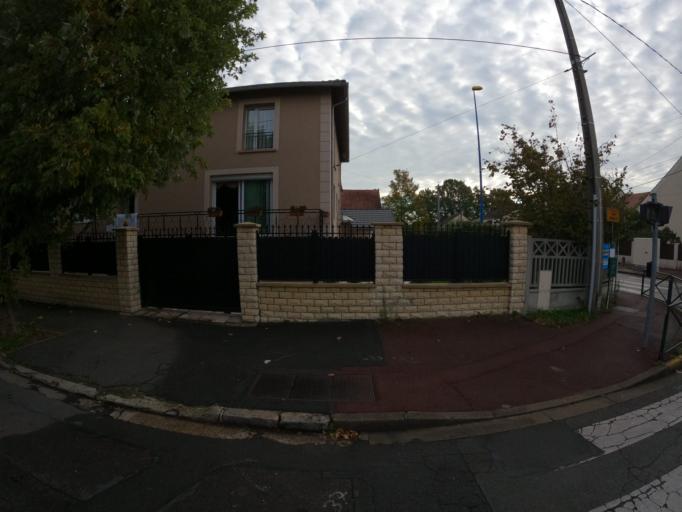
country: FR
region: Ile-de-France
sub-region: Departement de Seine-Saint-Denis
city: Montfermeil
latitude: 48.9025
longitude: 2.5953
